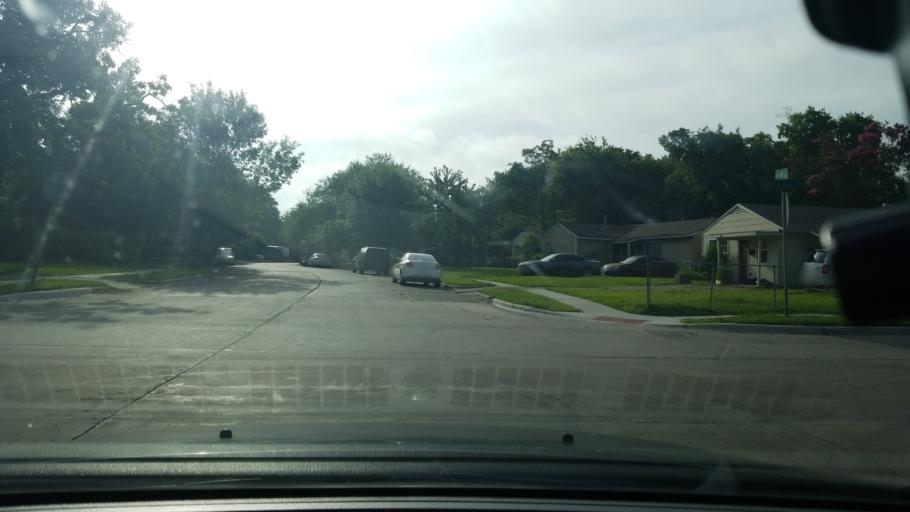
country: US
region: Texas
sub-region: Dallas County
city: Mesquite
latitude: 32.8268
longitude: -96.6638
